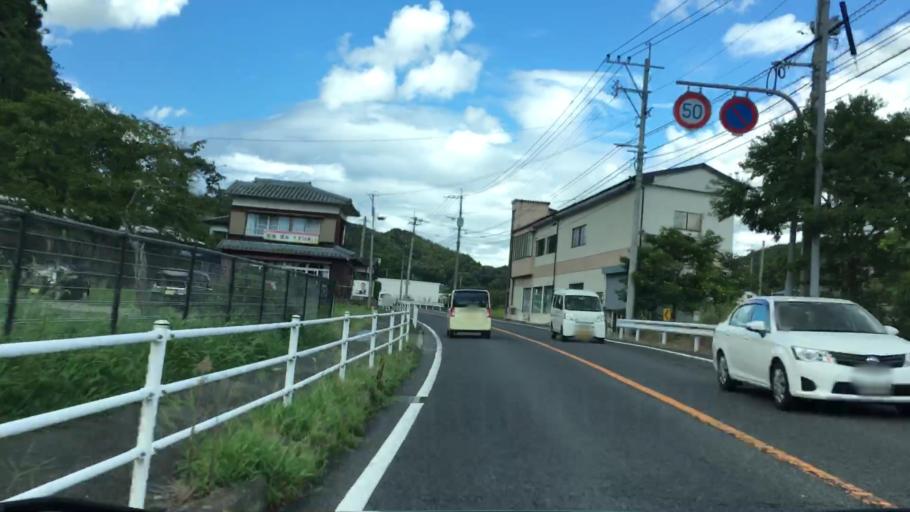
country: JP
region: Nagasaki
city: Sasebo
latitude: 33.1545
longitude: 129.8305
